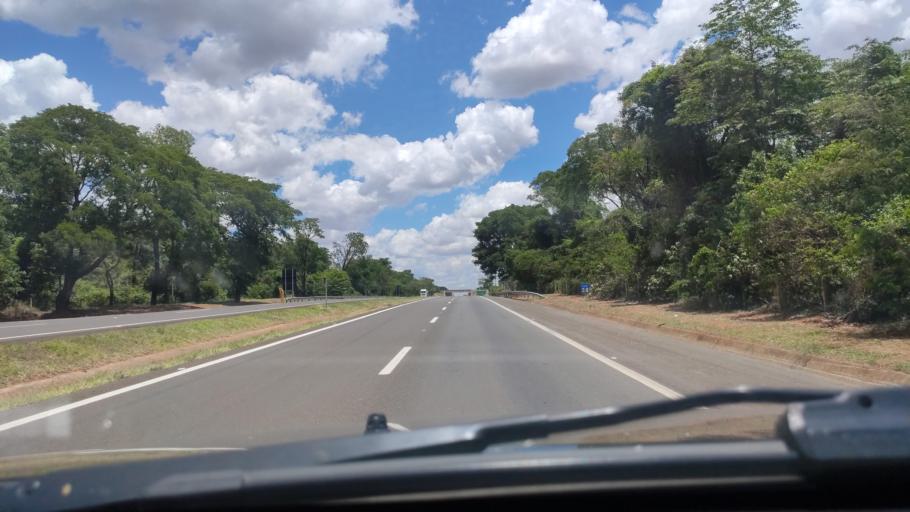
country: BR
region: Sao Paulo
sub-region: Bauru
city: Bauru
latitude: -22.3270
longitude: -48.9389
